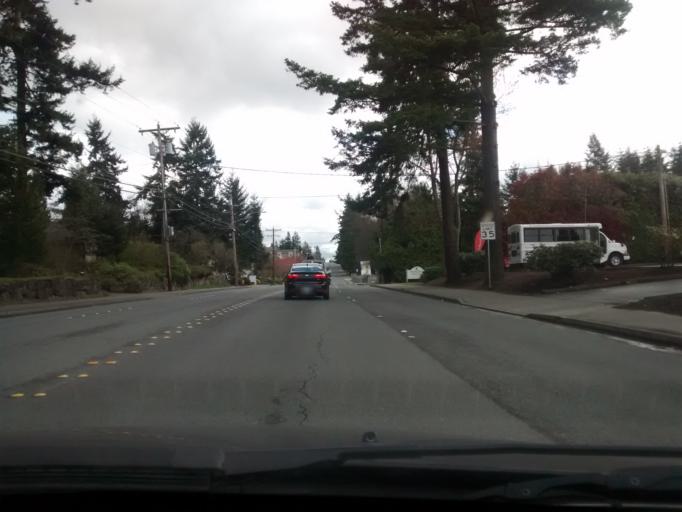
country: US
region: Washington
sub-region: Snohomish County
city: Lynnwood
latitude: 47.8215
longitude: -122.3338
